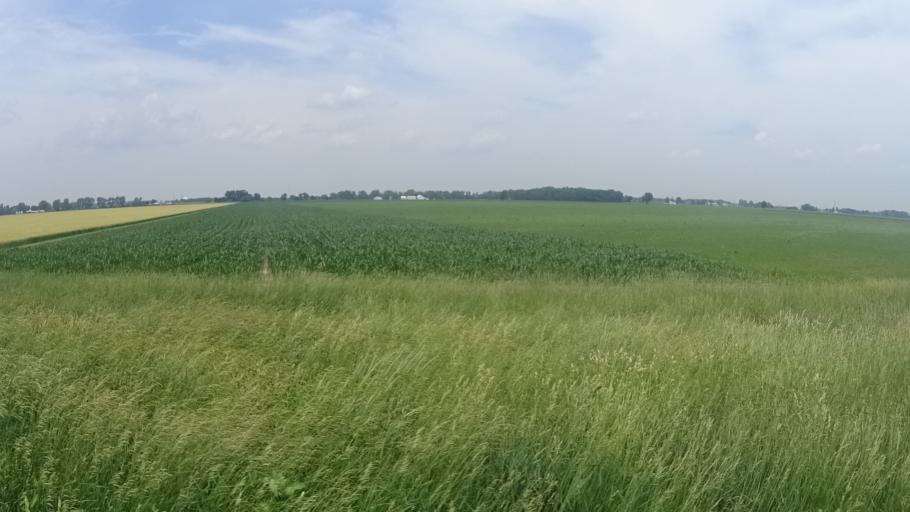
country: US
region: Ohio
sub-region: Erie County
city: Milan
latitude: 41.3104
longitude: -82.6426
